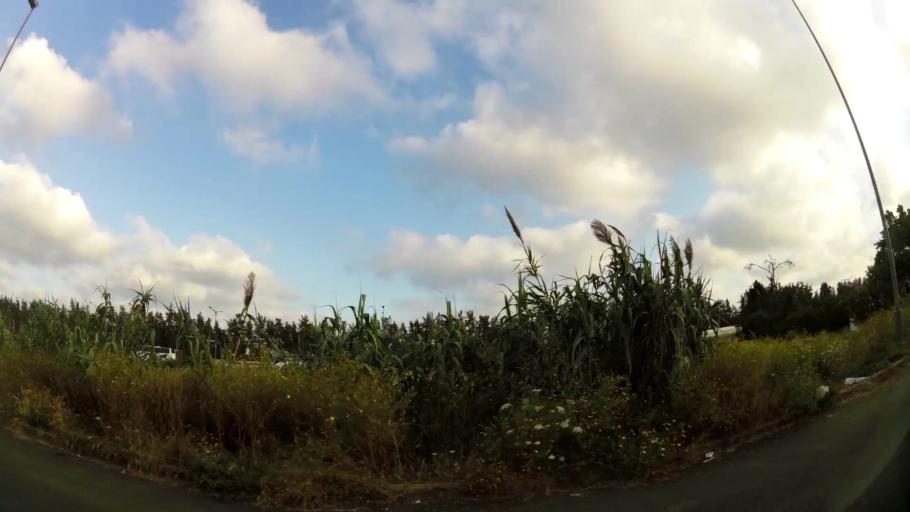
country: MA
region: Rabat-Sale-Zemmour-Zaer
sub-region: Rabat
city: Rabat
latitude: 33.9557
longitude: -6.8437
